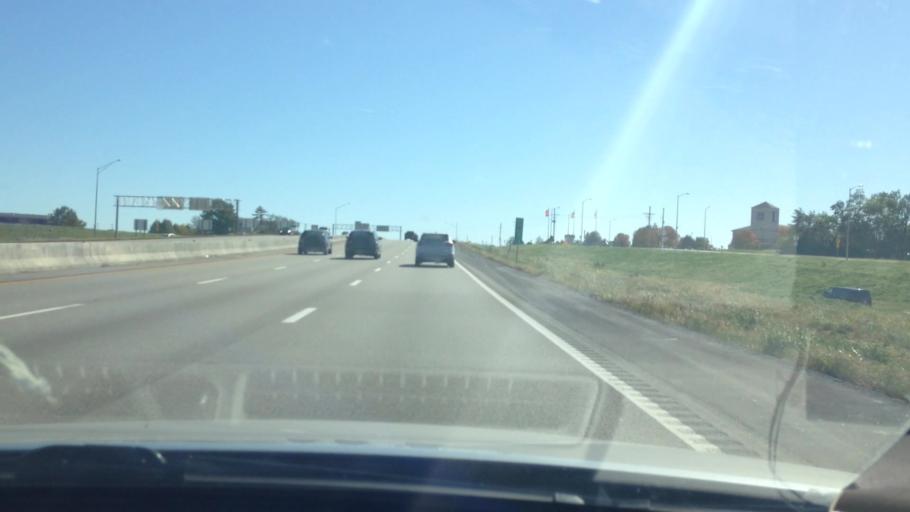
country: US
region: Missouri
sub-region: Platte County
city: Weatherby Lake
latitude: 39.2733
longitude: -94.6697
